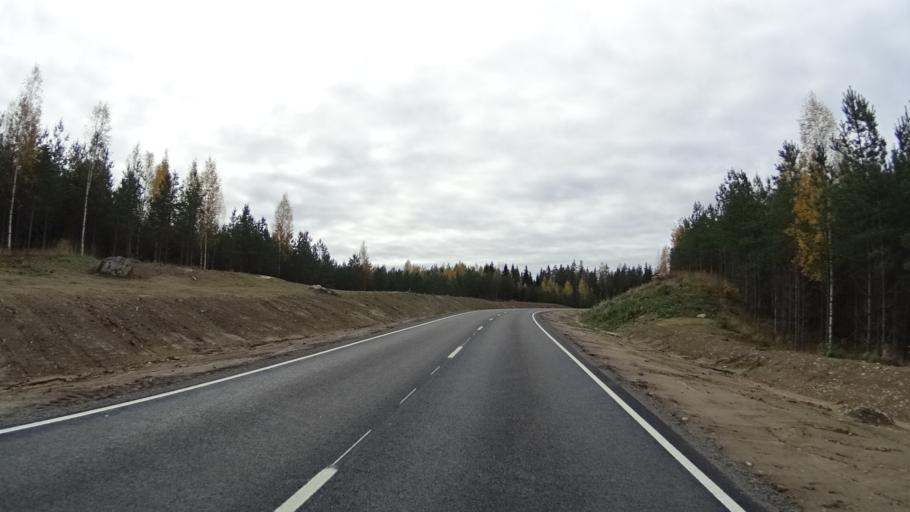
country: FI
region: South Karelia
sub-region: Lappeenranta
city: Taipalsaari
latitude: 61.0282
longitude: 28.0311
